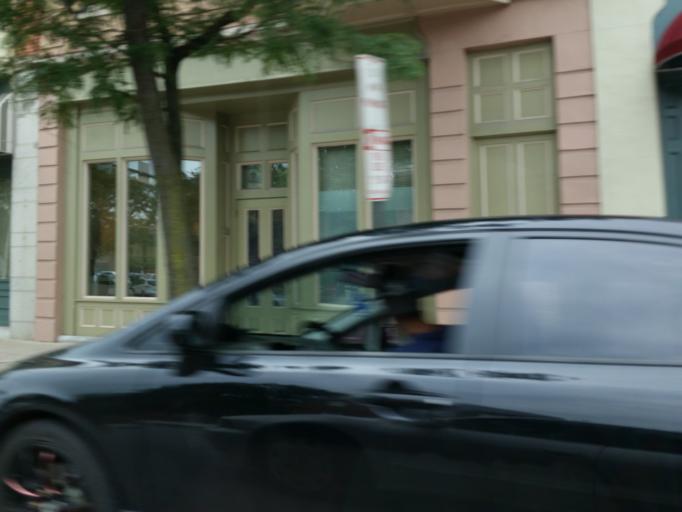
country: US
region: Pennsylvania
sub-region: York County
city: York
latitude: 39.9606
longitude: -76.7269
